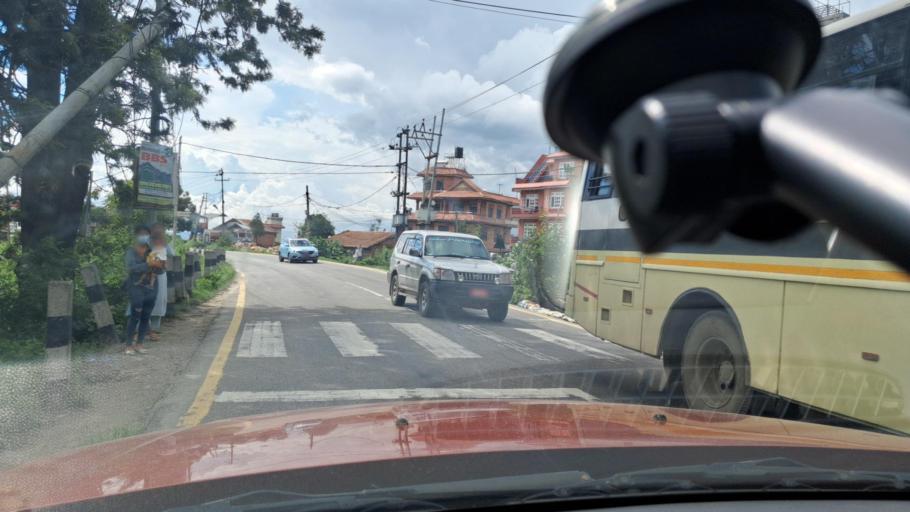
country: NP
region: Central Region
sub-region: Bagmati Zone
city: Hari Bdr Tamang House
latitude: 27.6534
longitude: 85.4599
